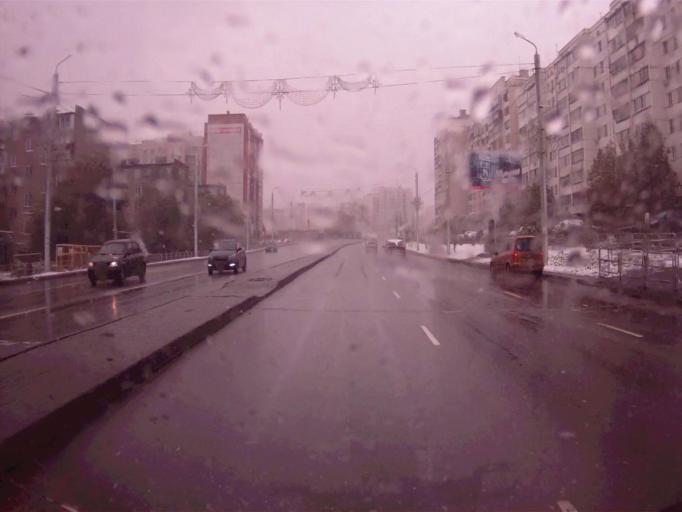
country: RU
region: Chelyabinsk
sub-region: Gorod Chelyabinsk
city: Chelyabinsk
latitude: 55.1428
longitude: 61.4095
